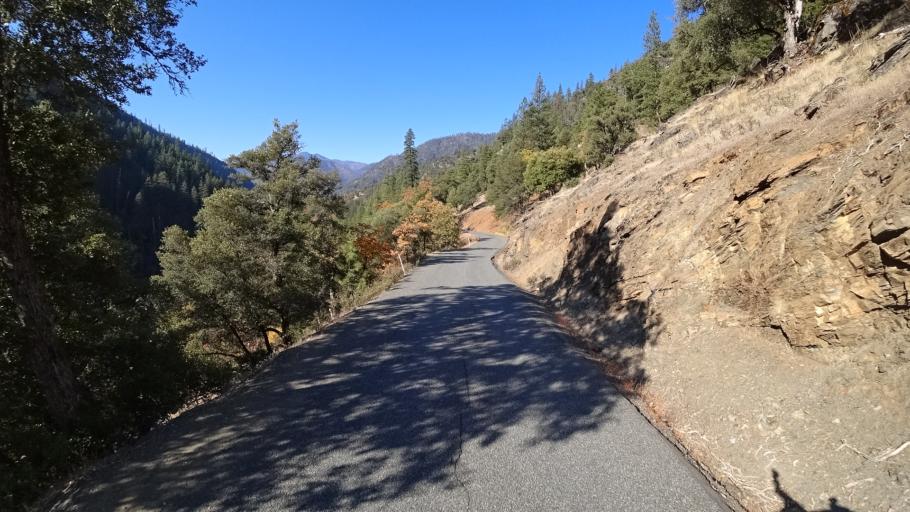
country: US
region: California
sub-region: Siskiyou County
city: Happy Camp
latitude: 41.6959
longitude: -123.0560
